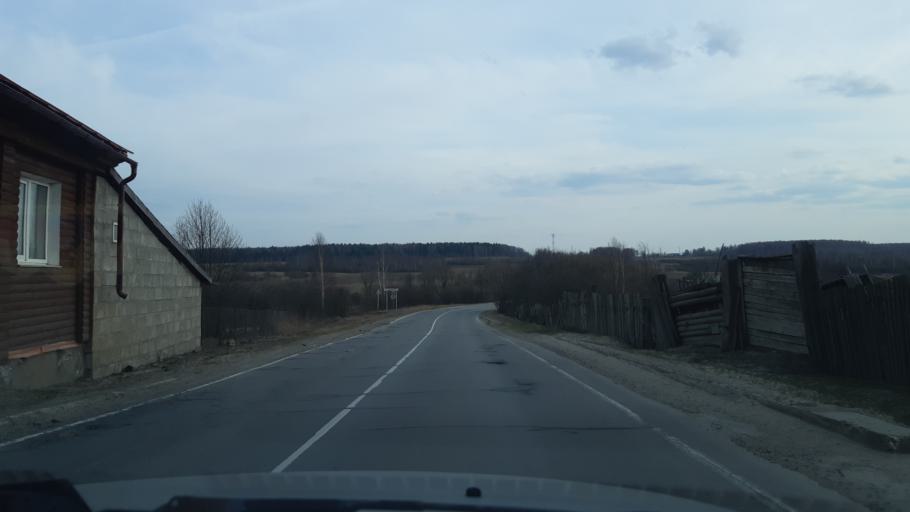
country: RU
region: Vladimir
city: Luknovo
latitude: 56.2143
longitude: 42.0303
